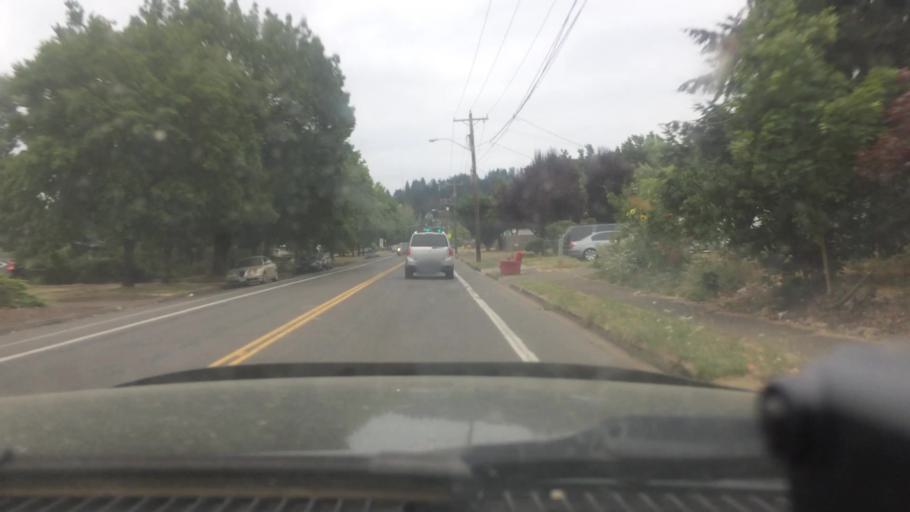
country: US
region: Oregon
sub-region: Lane County
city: Eugene
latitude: 44.0379
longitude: -123.1179
